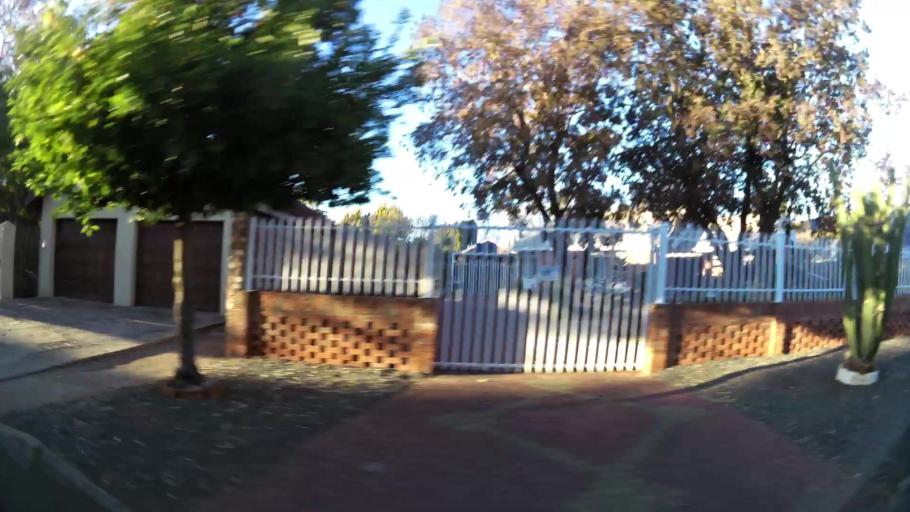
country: ZA
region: Northern Cape
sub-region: Frances Baard District Municipality
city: Kimberley
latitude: -28.7653
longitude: 24.7608
